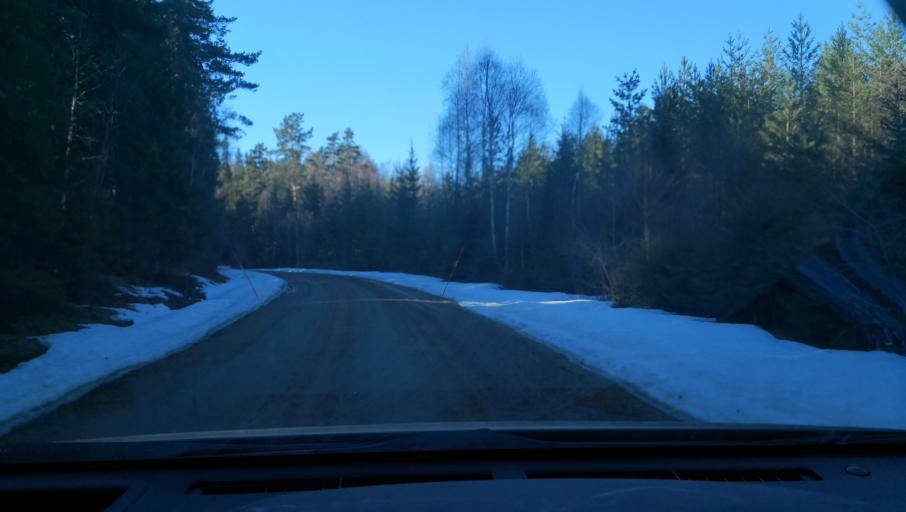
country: SE
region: Vaestmanland
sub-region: Sala Kommun
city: Sala
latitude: 60.1435
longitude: 16.6480
